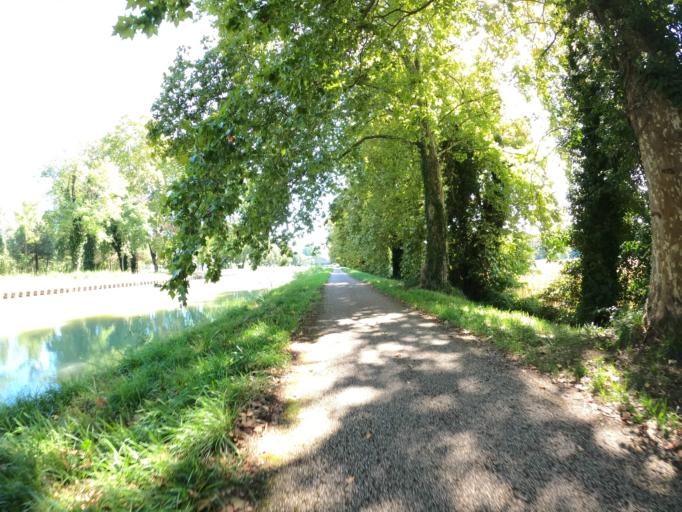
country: FR
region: Midi-Pyrenees
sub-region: Departement du Tarn-et-Garonne
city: Lamagistere
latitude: 44.1234
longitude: 0.8437
